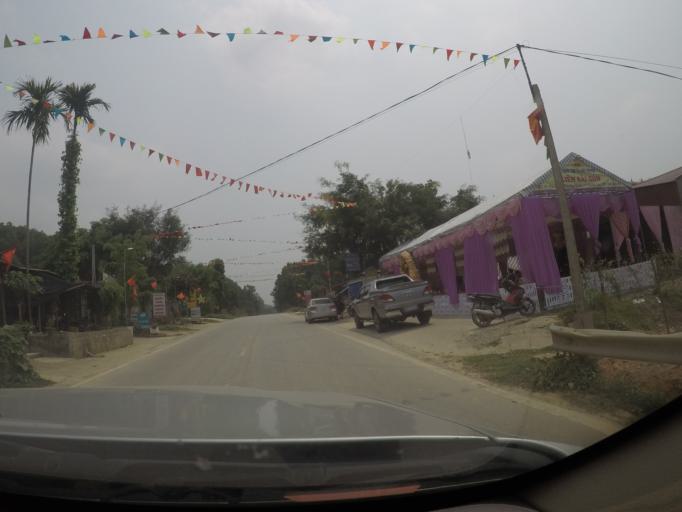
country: VN
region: Thanh Hoa
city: Thi Tran Yen Cat
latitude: 19.7656
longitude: 105.4141
